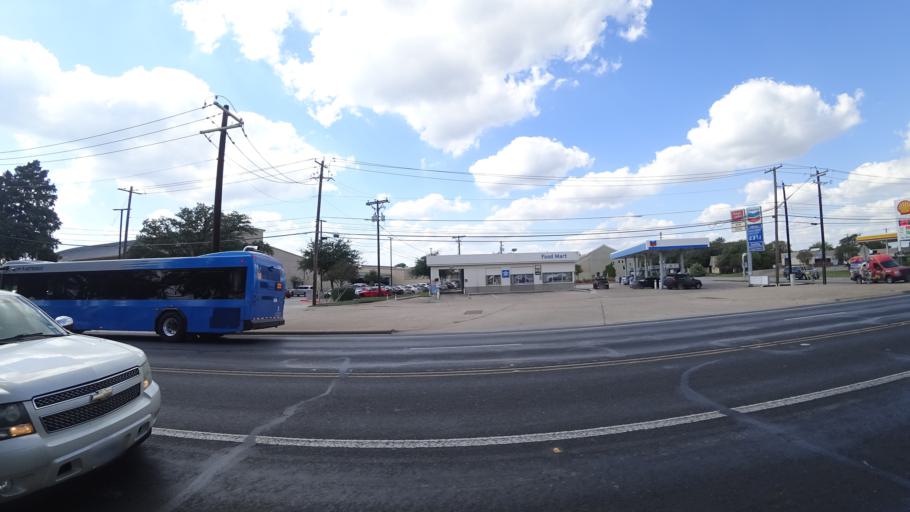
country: US
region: Texas
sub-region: Williamson County
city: Jollyville
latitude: 30.3615
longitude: -97.7294
